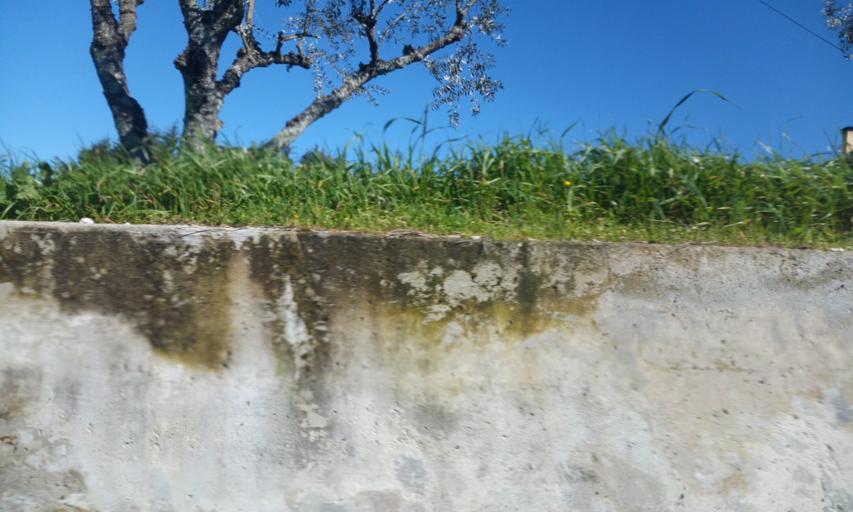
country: PT
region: Guarda
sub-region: Seia
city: Seia
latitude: 40.4706
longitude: -7.6227
